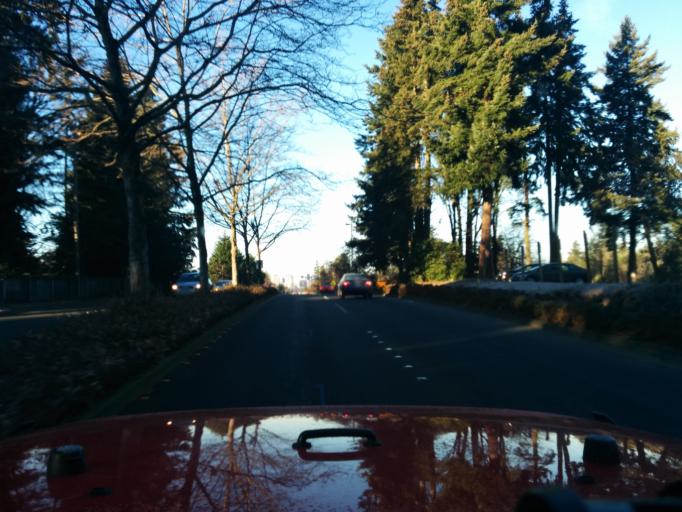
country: US
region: Washington
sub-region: King County
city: Eastgate
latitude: 47.6170
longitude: -122.1459
